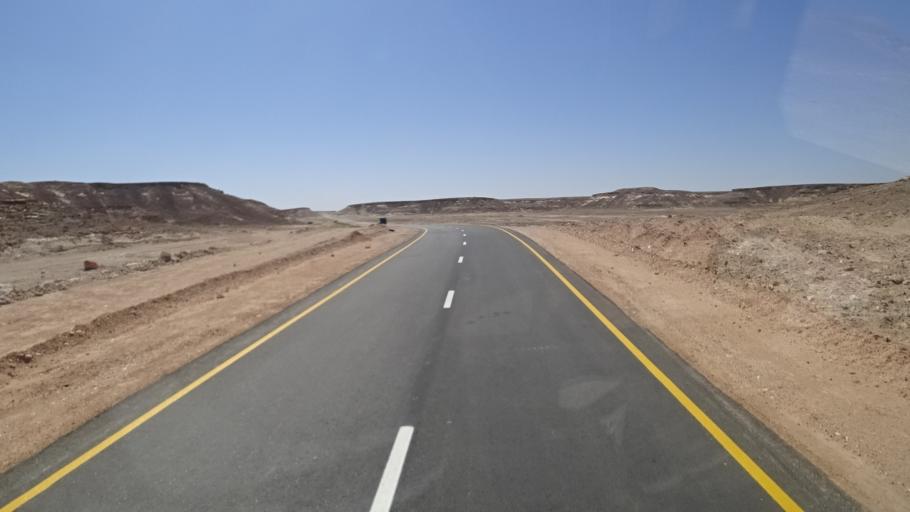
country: OM
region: Zufar
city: Salalah
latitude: 17.4749
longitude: 53.3488
